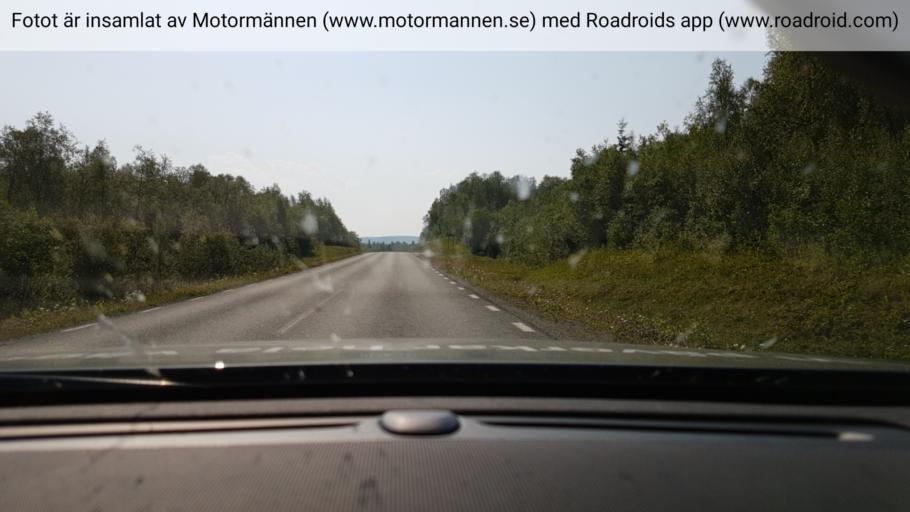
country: NO
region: Nordland
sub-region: Rana
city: Mo i Rana
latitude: 65.7728
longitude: 15.1127
